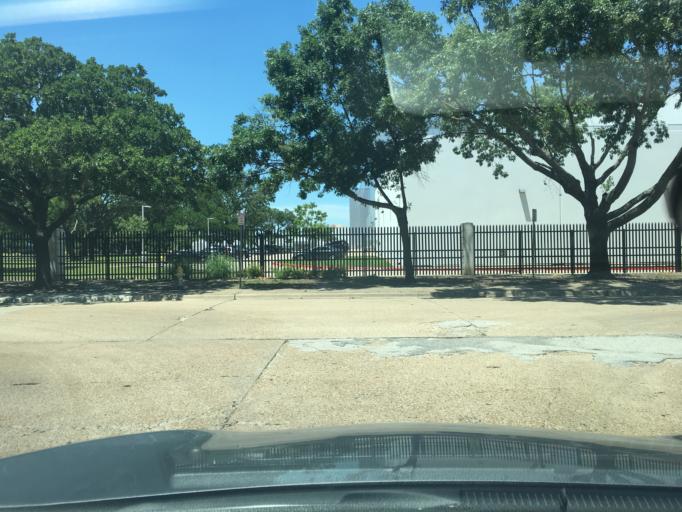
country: US
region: Texas
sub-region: Dallas County
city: Richardson
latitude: 32.9640
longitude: -96.7138
